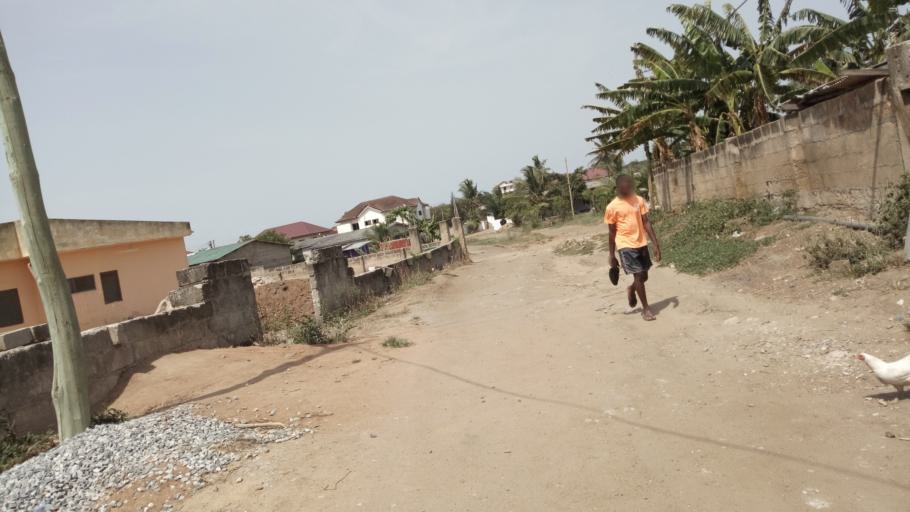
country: GH
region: Central
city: Winneba
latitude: 5.3588
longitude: -0.6369
